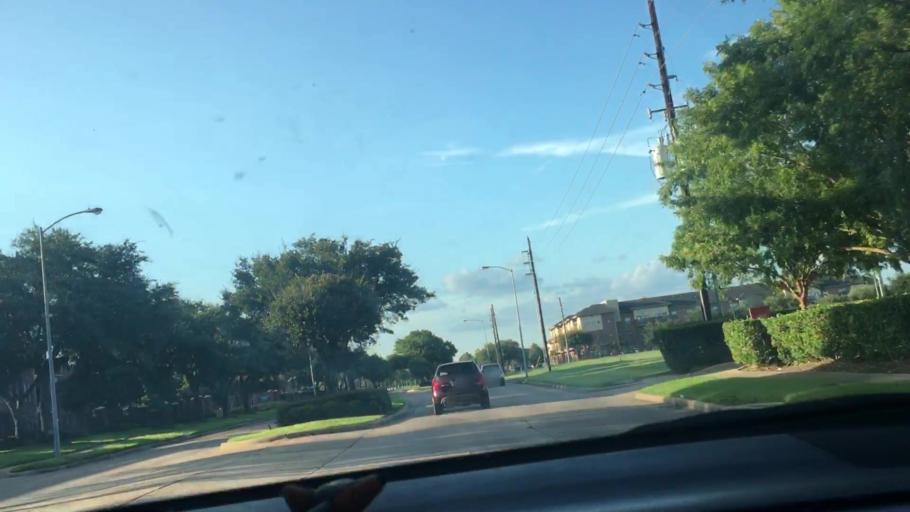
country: US
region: Texas
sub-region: Fort Bend County
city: Meadows Place
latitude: 29.6442
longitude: -95.5820
